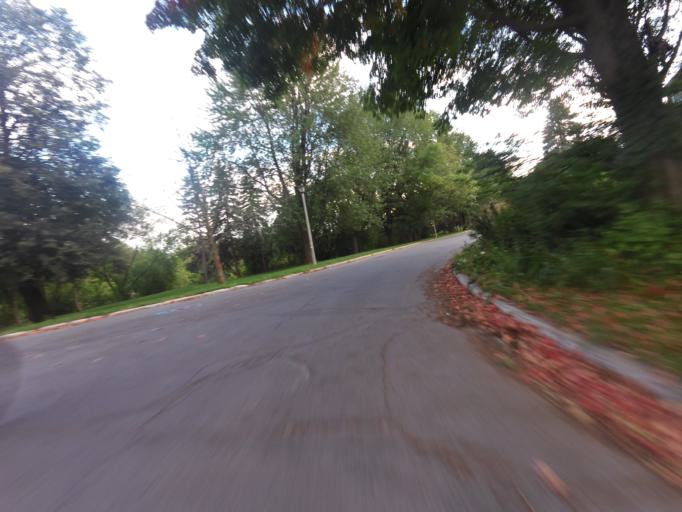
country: CA
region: Ontario
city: Ottawa
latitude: 45.3996
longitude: -75.6726
